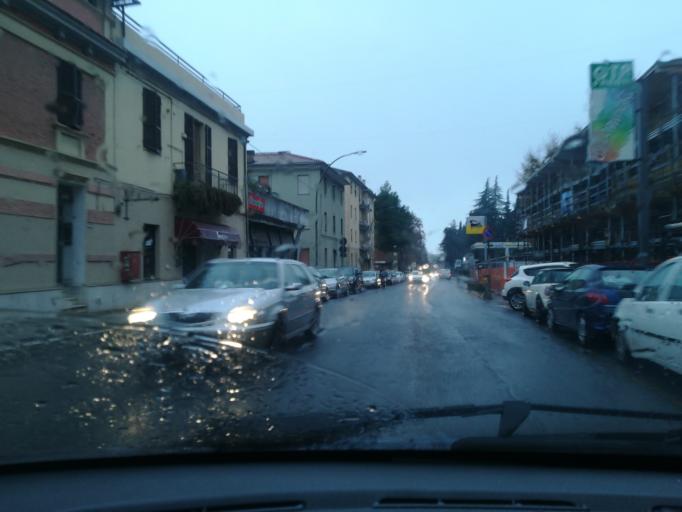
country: IT
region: The Marches
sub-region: Provincia di Macerata
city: Macerata
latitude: 43.2974
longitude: 13.4384
